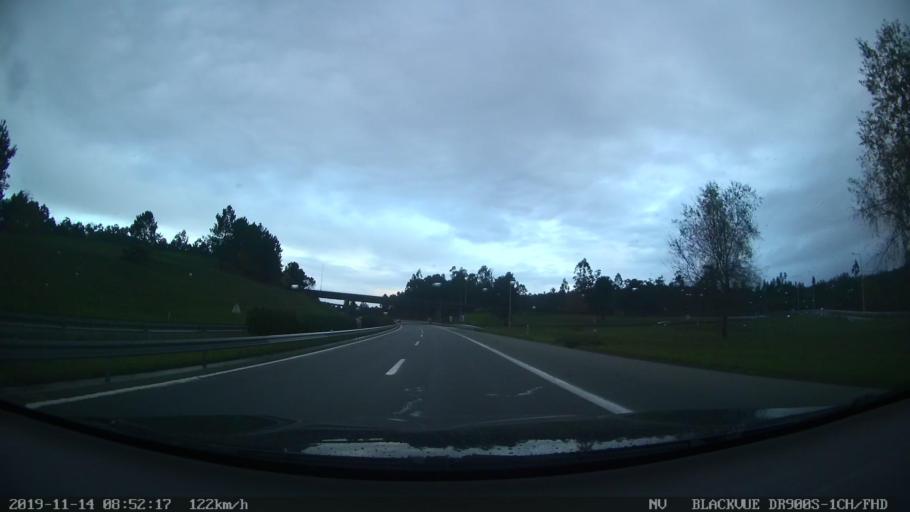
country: PT
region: Viana do Castelo
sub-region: Vila Nova de Cerveira
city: Vila Nova de Cerveira
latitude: 41.9246
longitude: -8.6525
